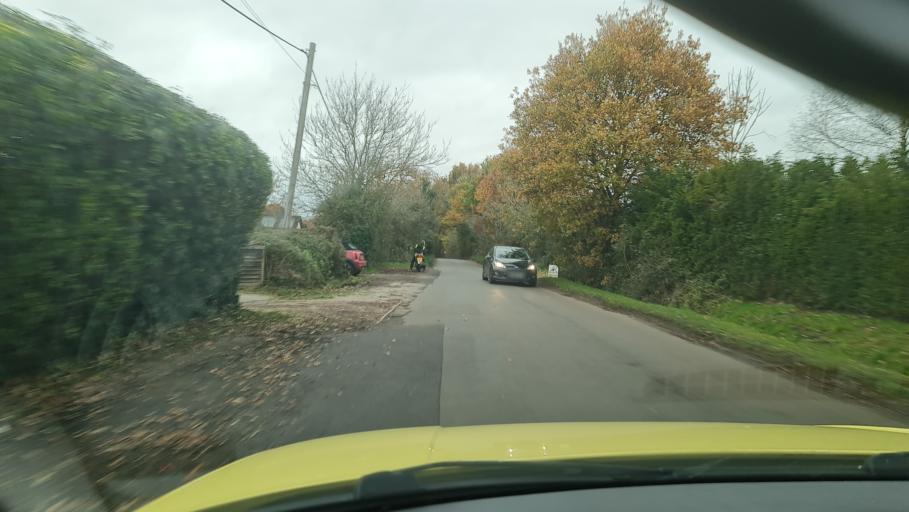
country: GB
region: England
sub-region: Hampshire
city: Yateley
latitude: 51.3503
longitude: -0.8176
